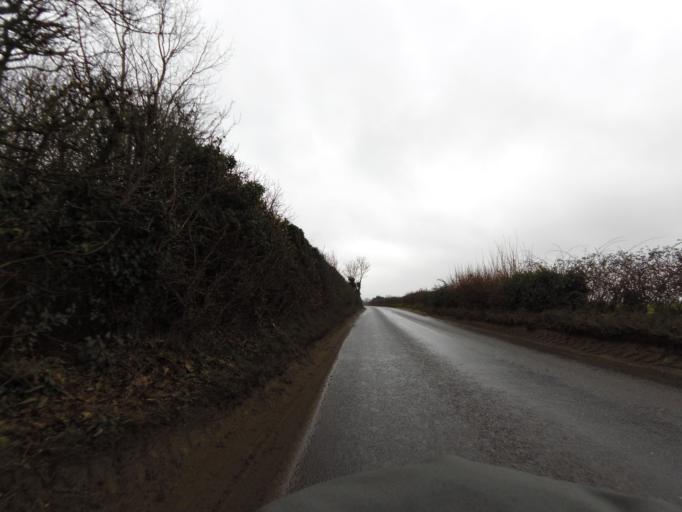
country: GB
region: England
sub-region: Norfolk
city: Briston
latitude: 52.8970
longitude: 1.0883
